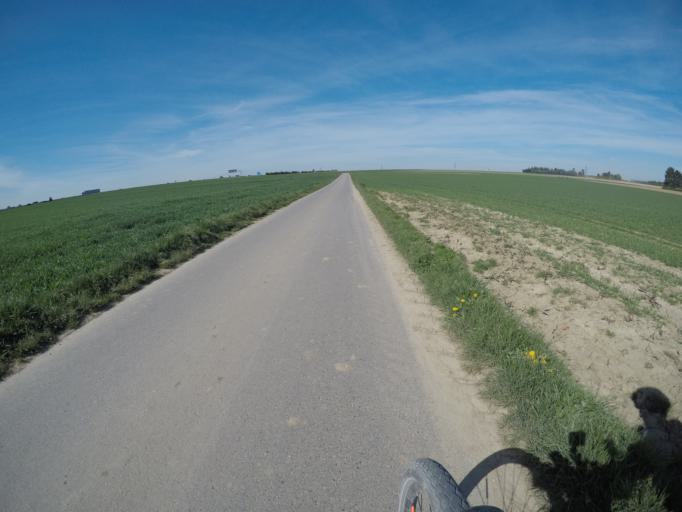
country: DE
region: Baden-Wuerttemberg
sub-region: Regierungsbezirk Stuttgart
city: Korntal
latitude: 48.8577
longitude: 9.1292
